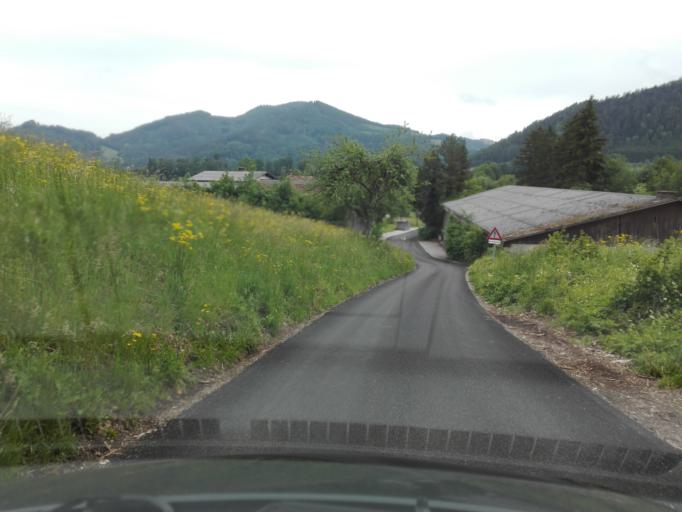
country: AT
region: Upper Austria
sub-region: Politischer Bezirk Gmunden
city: Scharnstein
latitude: 47.9176
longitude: 13.9682
